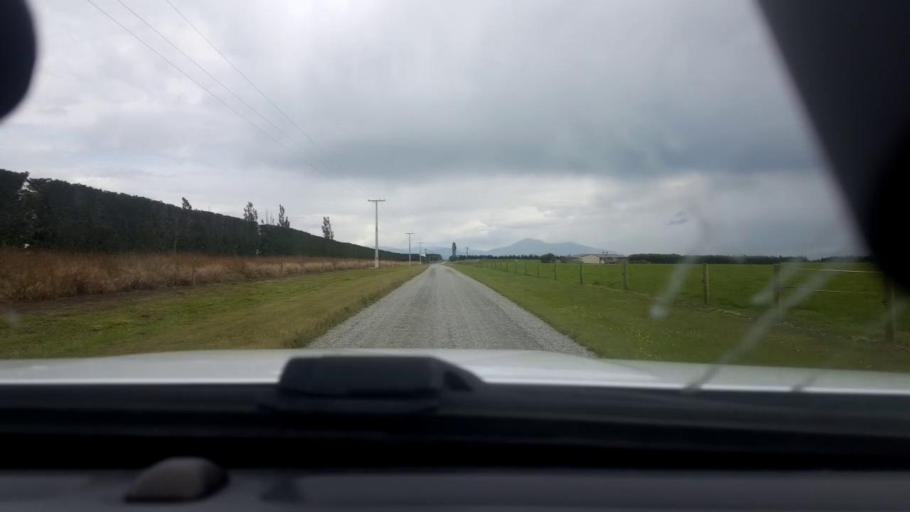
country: NZ
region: Canterbury
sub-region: Timaru District
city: Timaru
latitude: -44.1750
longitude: 171.4192
